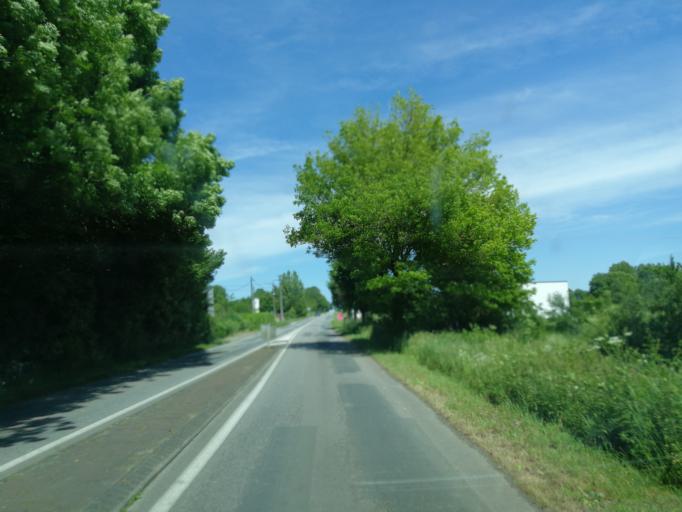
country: FR
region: Poitou-Charentes
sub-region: Departement des Deux-Sevres
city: Courlay
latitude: 46.8018
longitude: -0.5801
